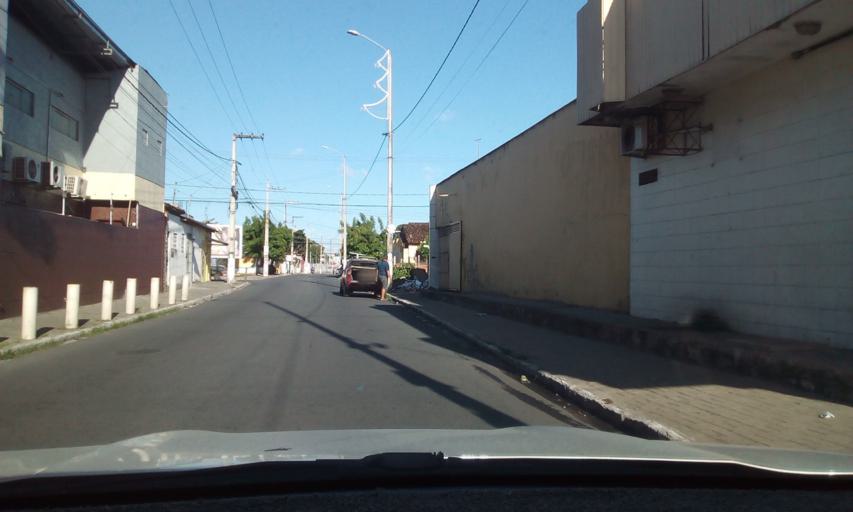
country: BR
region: Paraiba
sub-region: Bayeux
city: Bayeux
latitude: -7.1257
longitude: -34.9220
